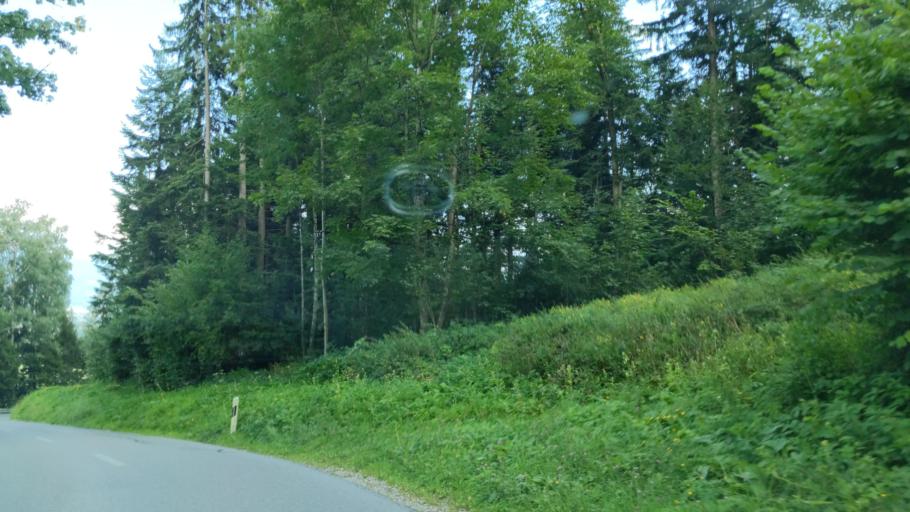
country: CH
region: Saint Gallen
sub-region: Wahlkreis Rheintal
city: Eichberg
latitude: 47.3427
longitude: 9.5130
